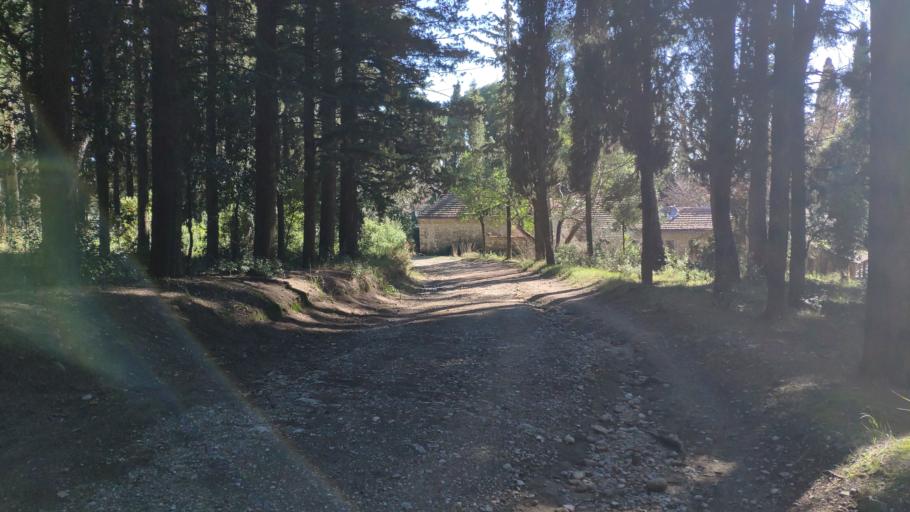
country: GR
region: Attica
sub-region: Nomarchia Anatolikis Attikis
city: Varybobi
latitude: 38.1595
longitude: 23.7959
